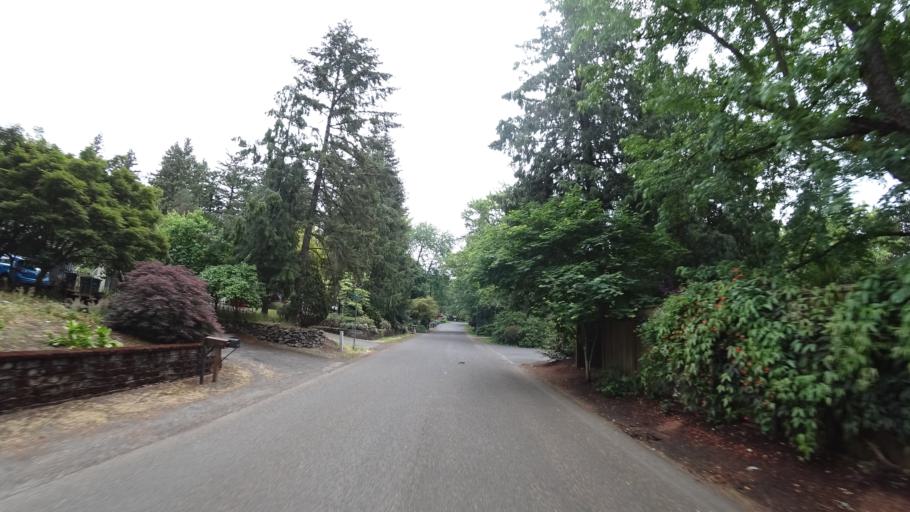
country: US
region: Oregon
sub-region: Washington County
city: Garden Home-Whitford
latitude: 45.4726
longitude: -122.7449
